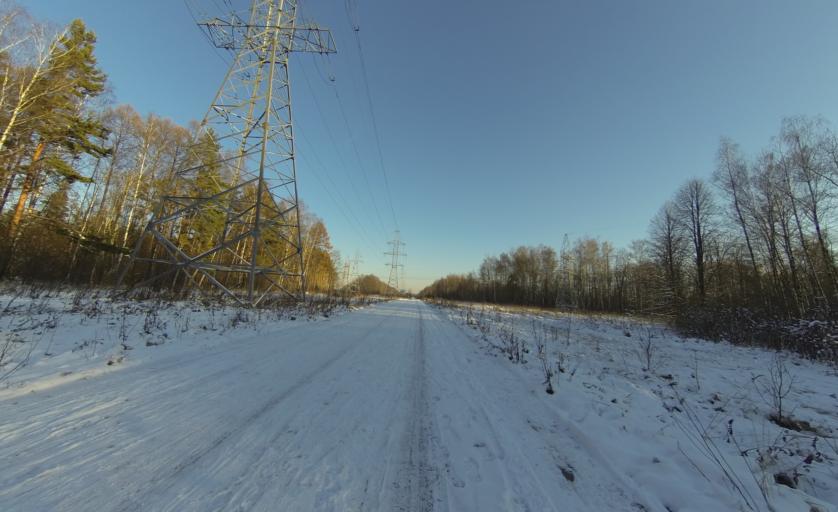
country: RU
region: Moscow
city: Babushkin
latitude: 55.8426
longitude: 37.7421
